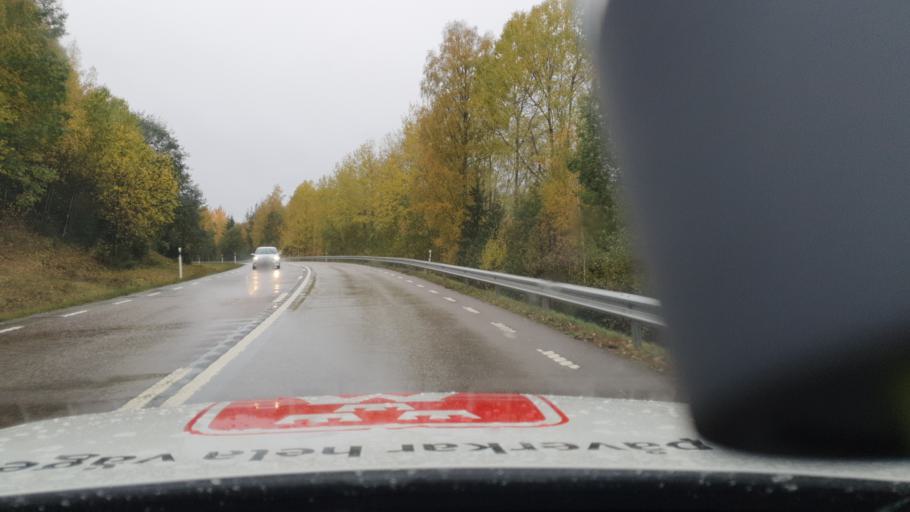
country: SE
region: Vaestra Goetaland
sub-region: Bengtsfors Kommun
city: Billingsfors
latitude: 58.9411
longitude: 12.1107
